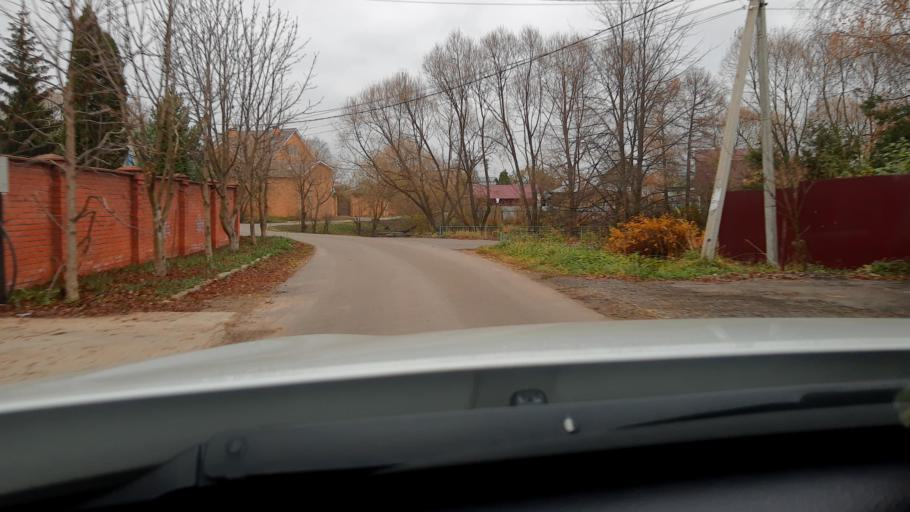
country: RU
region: Moscow
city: Tolstopal'tsevo
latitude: 55.6029
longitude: 37.2313
